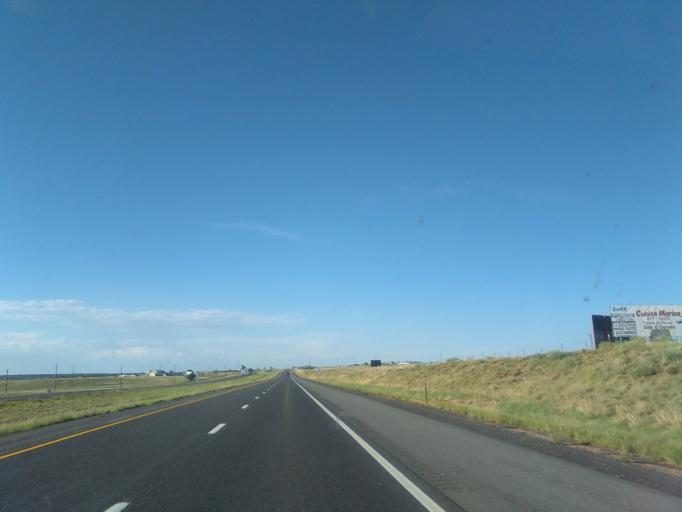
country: US
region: New Mexico
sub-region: San Miguel County
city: Las Vegas
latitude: 35.6320
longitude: -105.2010
